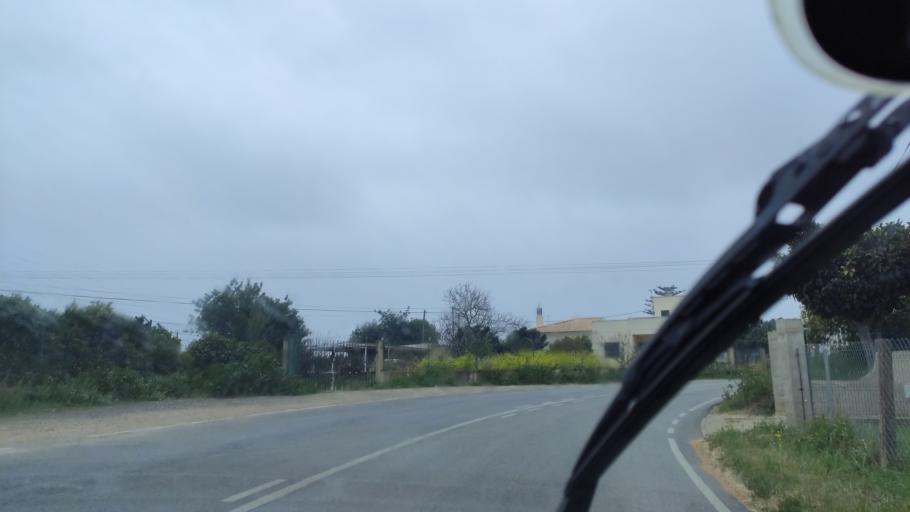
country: PT
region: Faro
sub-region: Faro
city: Santa Barbara de Nexe
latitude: 37.0749
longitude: -7.9340
